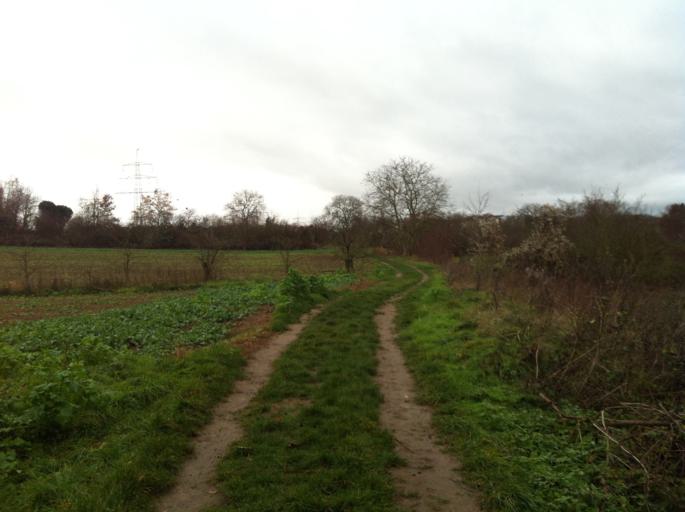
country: DE
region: Rheinland-Pfalz
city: Budenheim
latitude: 49.9956
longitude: 8.2008
